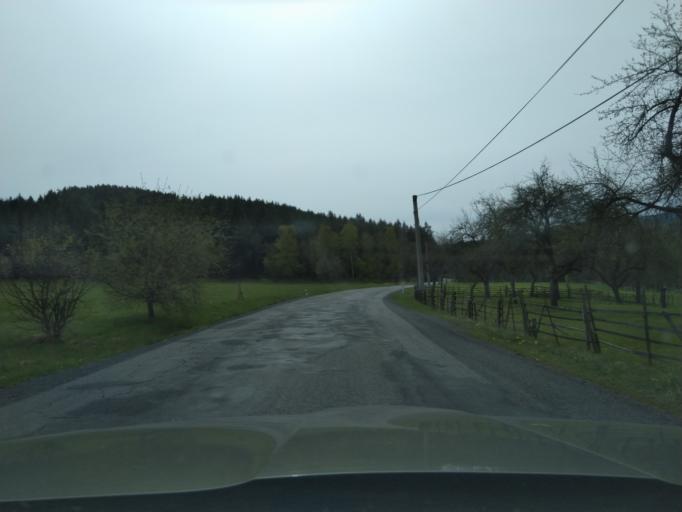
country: CZ
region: Plzensky
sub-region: Okres Klatovy
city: Kasperske Hory
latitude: 49.1914
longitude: 13.6241
